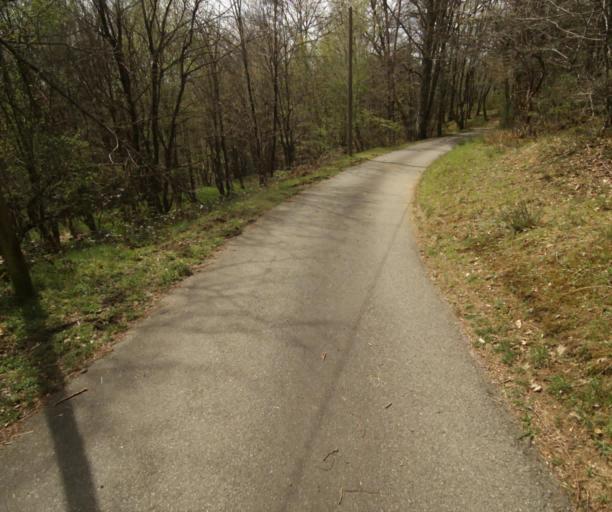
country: FR
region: Limousin
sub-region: Departement de la Correze
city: Argentat
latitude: 45.1899
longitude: 1.8868
